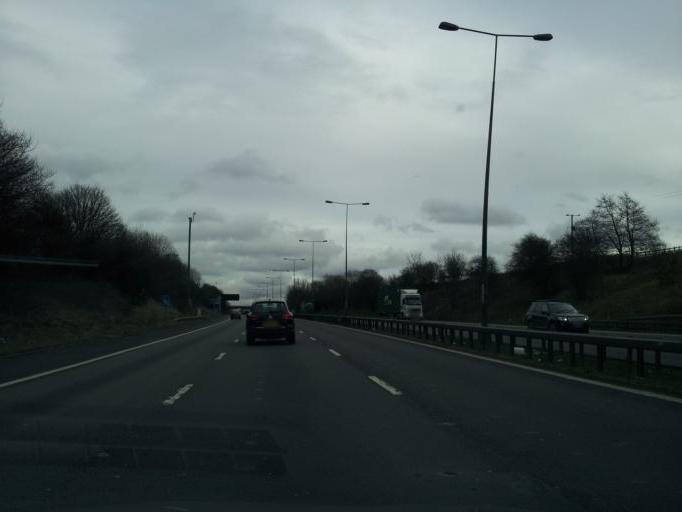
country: GB
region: England
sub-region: Staffordshire
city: Audley
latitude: 52.9939
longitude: -2.3004
